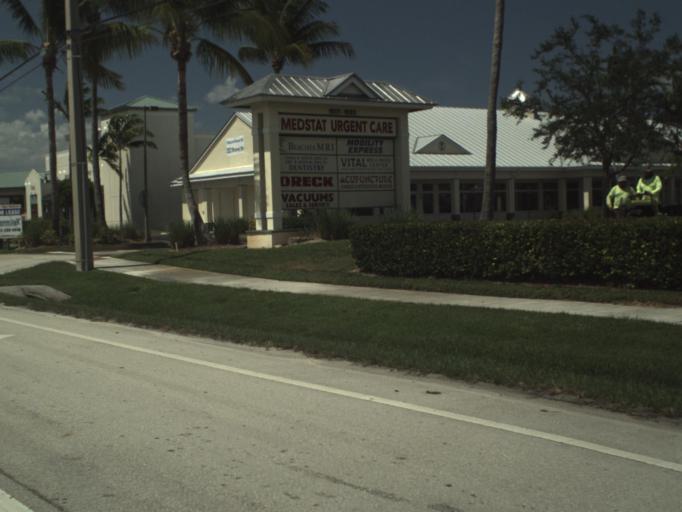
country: US
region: Florida
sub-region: Martin County
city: North River Shores
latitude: 27.2250
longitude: -80.2644
